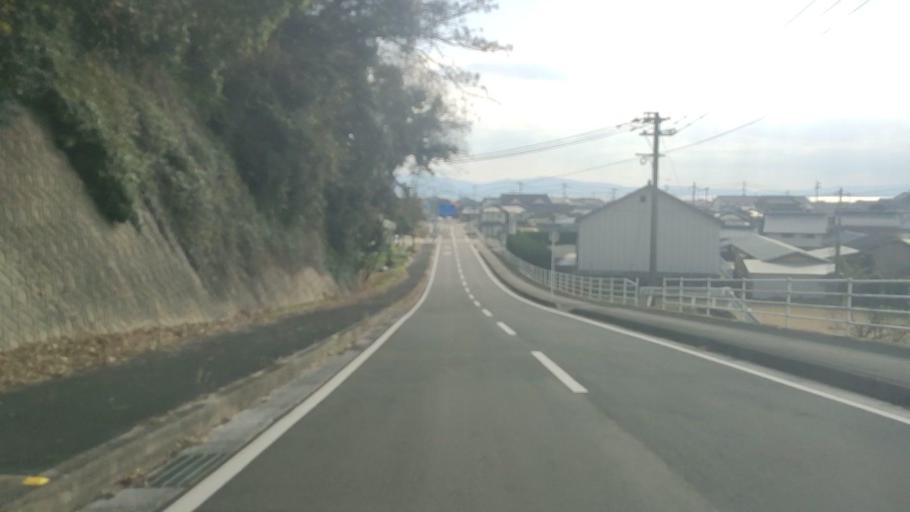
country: JP
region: Nagasaki
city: Shimabara
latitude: 32.6568
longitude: 130.2883
